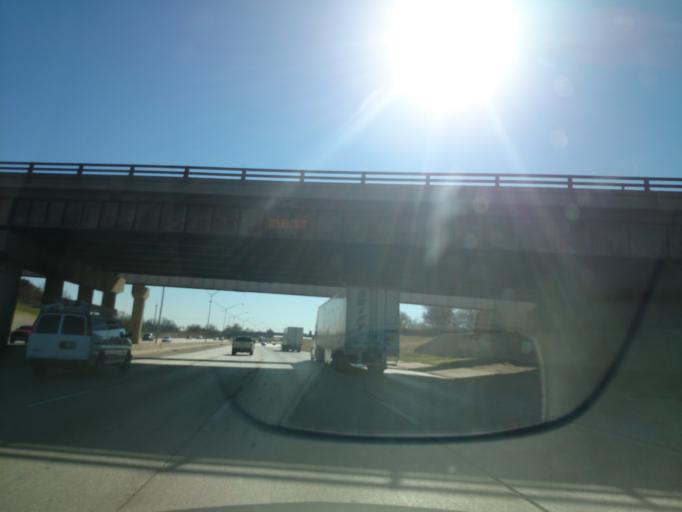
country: US
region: Oklahoma
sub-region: Oklahoma County
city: Warr Acres
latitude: 35.4861
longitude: -97.5796
